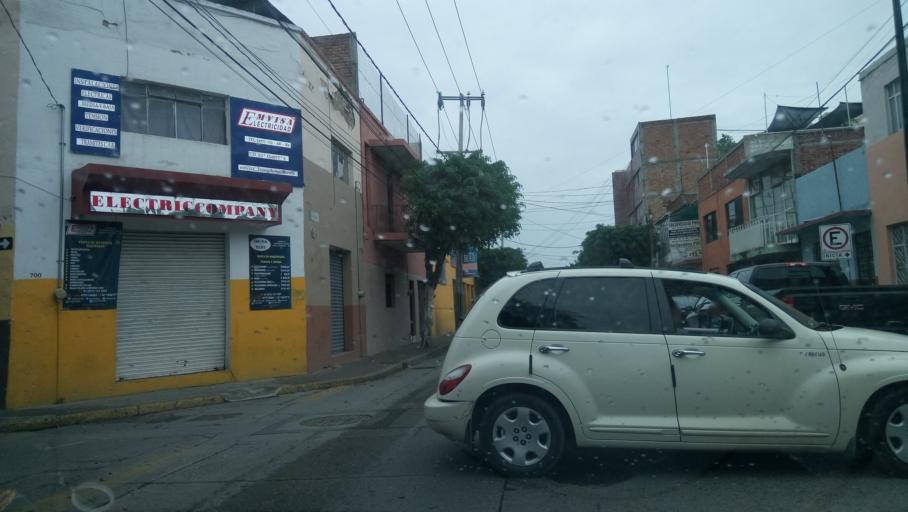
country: MX
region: Guanajuato
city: Leon
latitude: 21.1188
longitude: -101.6750
